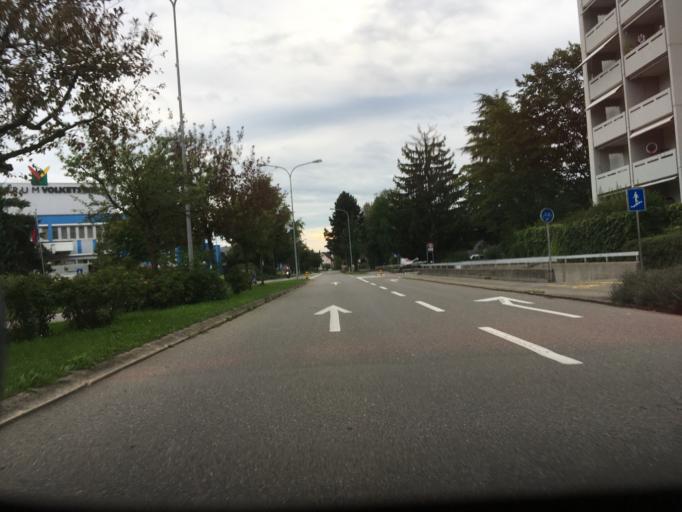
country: CH
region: Zurich
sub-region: Bezirk Uster
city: Hegnau / Sunnebueel-Eich
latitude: 47.3892
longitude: 8.6817
